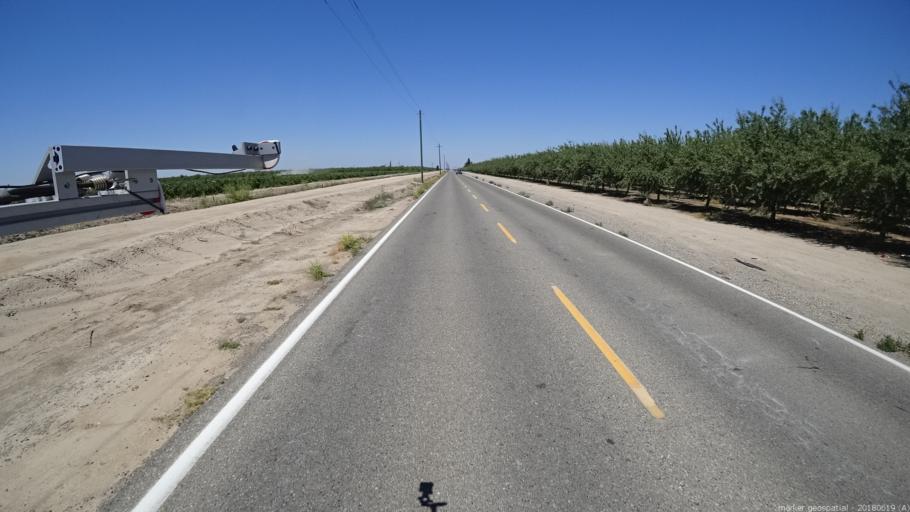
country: US
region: California
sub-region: Madera County
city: Parkwood
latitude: 36.8512
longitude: -120.1026
